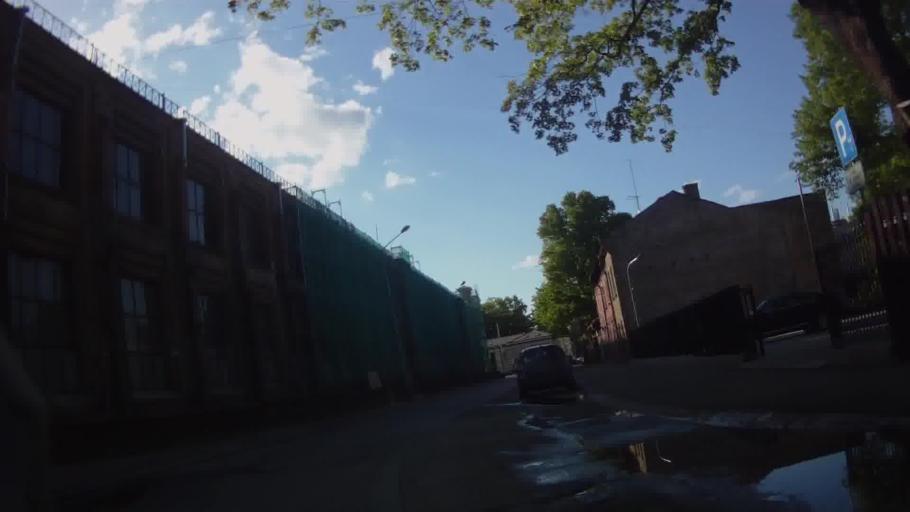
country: LV
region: Riga
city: Riga
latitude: 56.9709
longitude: 24.1624
